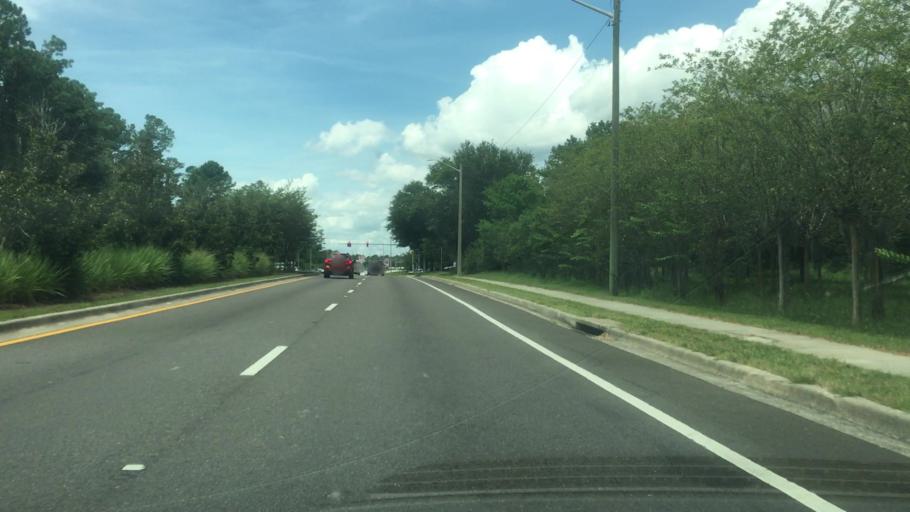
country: US
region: Florida
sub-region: Duval County
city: Jacksonville
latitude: 30.3548
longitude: -81.5440
